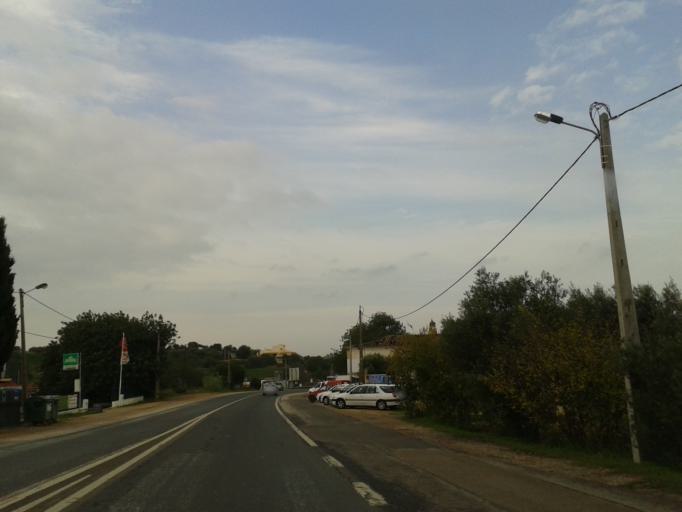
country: PT
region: Faro
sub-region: Loule
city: Boliqueime
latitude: 37.1268
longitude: -8.1608
